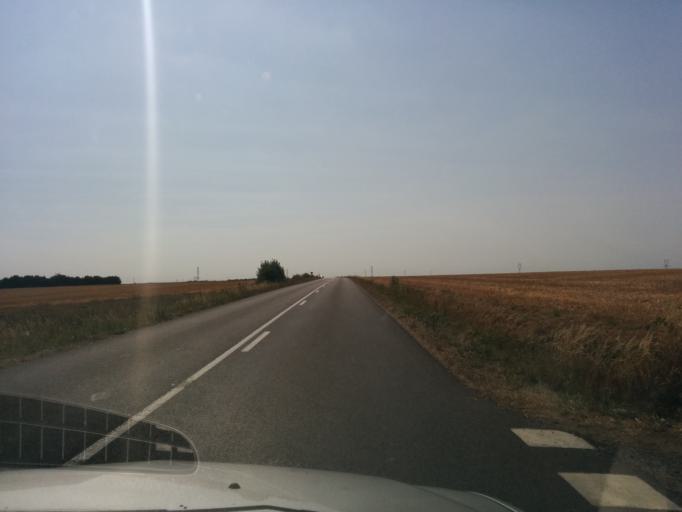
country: FR
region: Poitou-Charentes
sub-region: Departement de la Vienne
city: Moncontour
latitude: 46.8109
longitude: -0.0475
